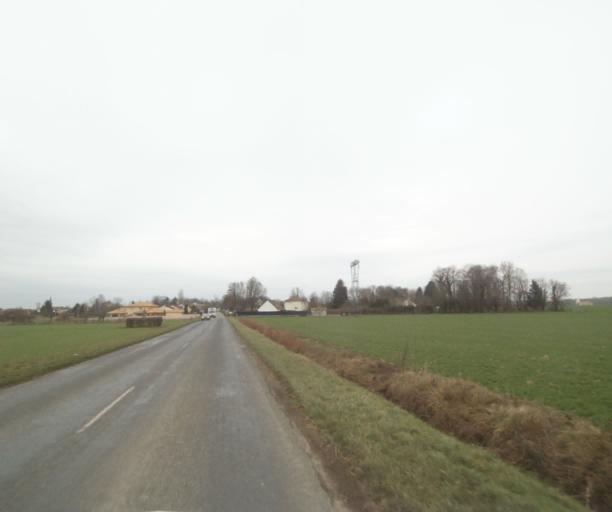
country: FR
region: Champagne-Ardenne
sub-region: Departement de la Haute-Marne
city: Villiers-en-Lieu
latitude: 48.6615
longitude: 4.9076
